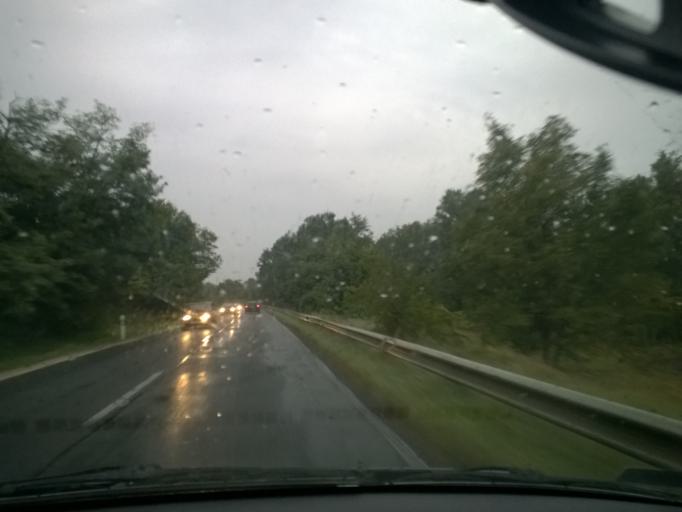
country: HU
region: Pest
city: Domsod
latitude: 47.1236
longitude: 19.0035
